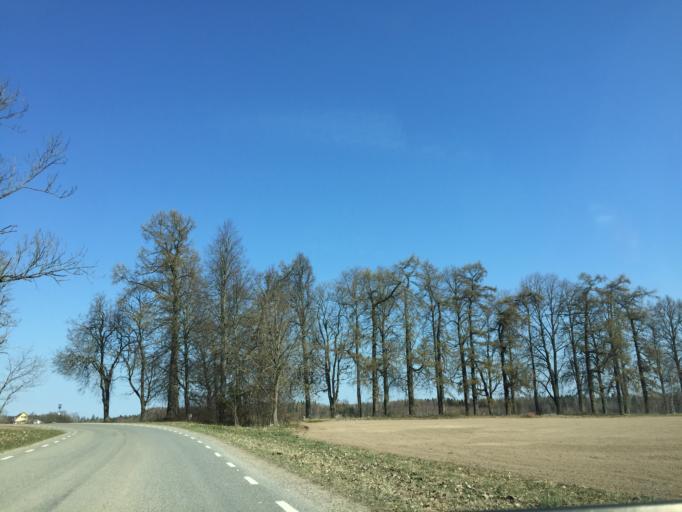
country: EE
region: Tartu
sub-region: Tartu linn
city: Tartu
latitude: 58.5271
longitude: 26.8767
